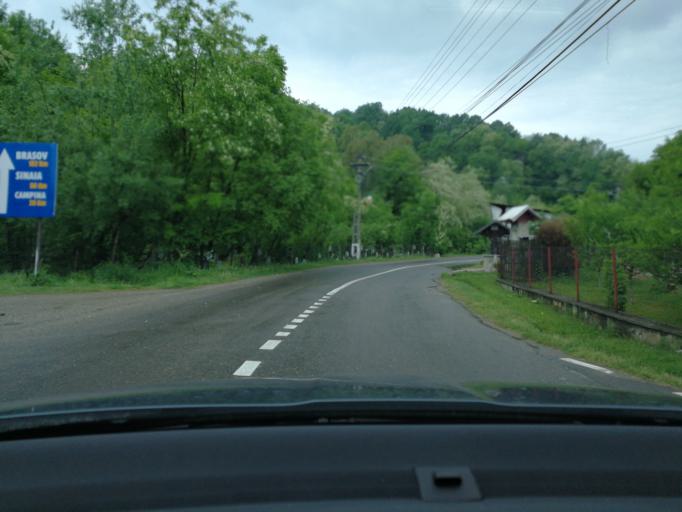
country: RO
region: Prahova
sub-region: Comuna Alunis
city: Ostrovu
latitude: 45.1990
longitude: 25.8956
